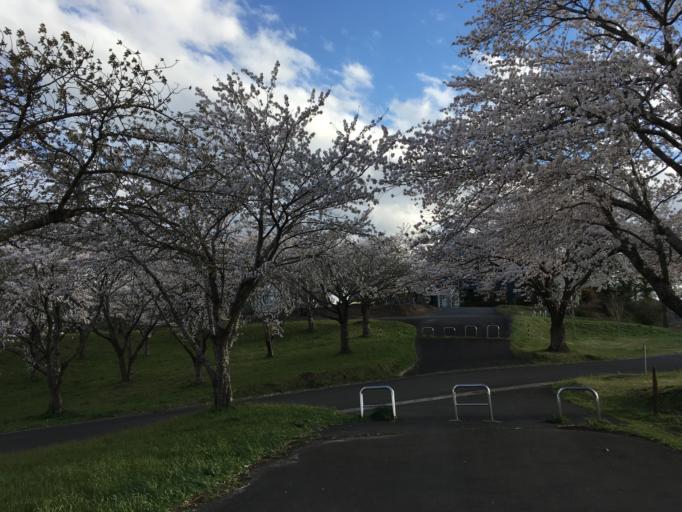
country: JP
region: Miyagi
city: Wakuya
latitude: 38.6895
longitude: 141.1340
